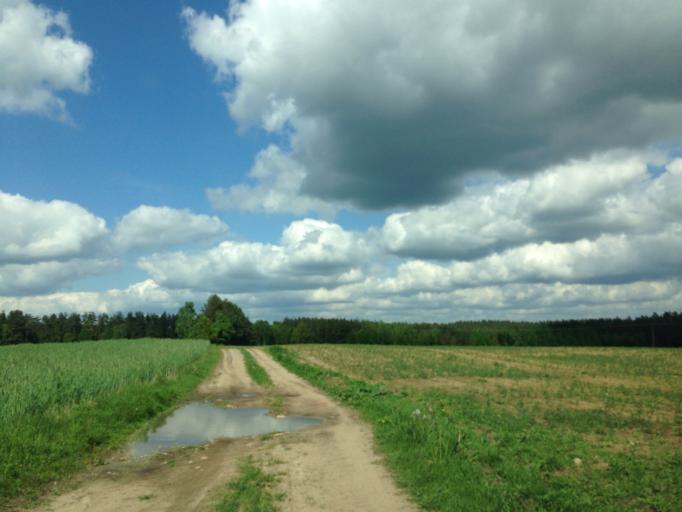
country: PL
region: Warmian-Masurian Voivodeship
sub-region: Powiat nidzicki
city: Nidzica
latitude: 53.4467
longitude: 20.3426
